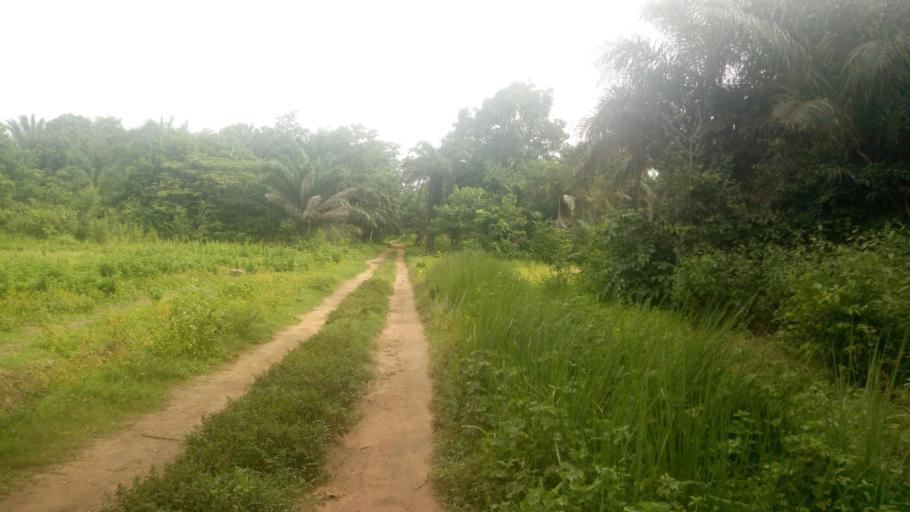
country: SL
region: Northern Province
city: Magburaka
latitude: 8.6769
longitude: -12.0313
